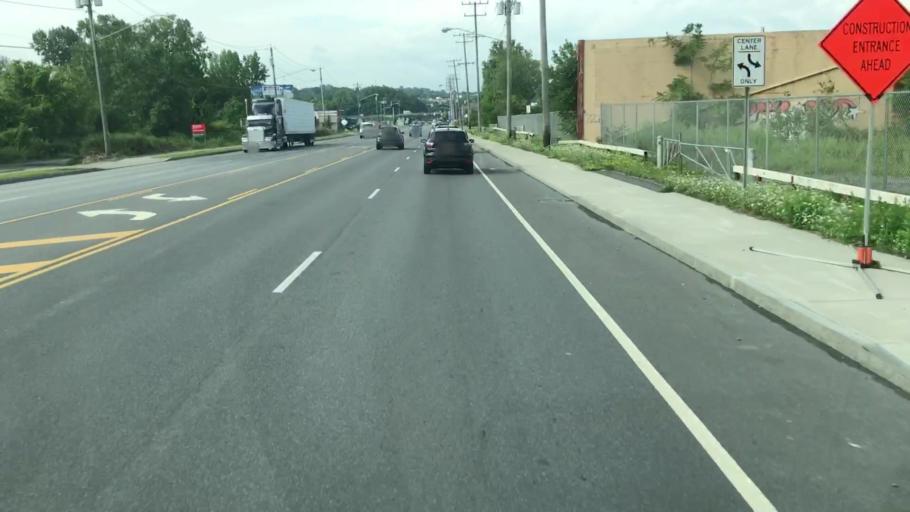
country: US
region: New York
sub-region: Onondaga County
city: Galeville
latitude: 43.0618
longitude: -76.1772
